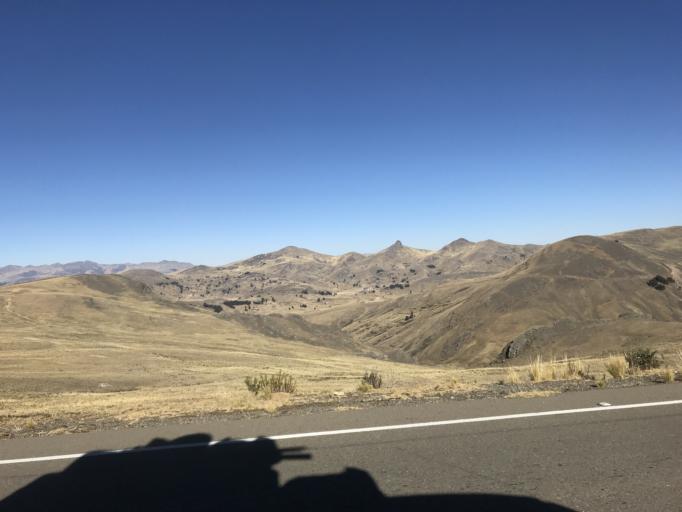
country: PE
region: Puno
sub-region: Yunguyo
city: Yunguyo
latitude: -16.1619
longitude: -68.9901
